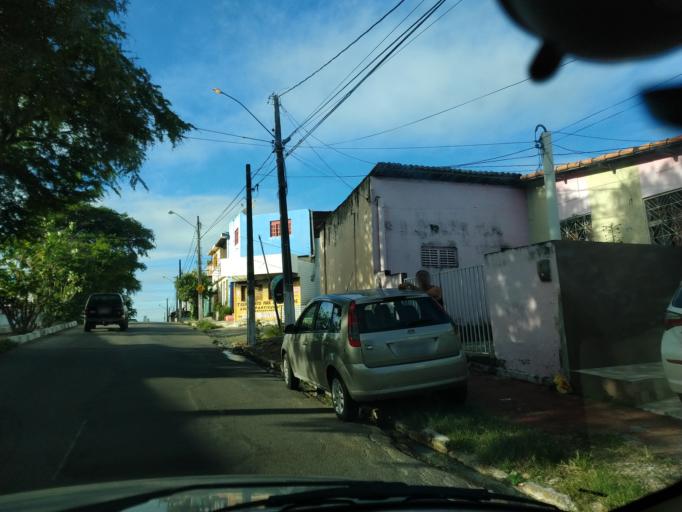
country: BR
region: Rio Grande do Norte
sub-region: Natal
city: Natal
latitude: -5.8068
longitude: -35.2139
